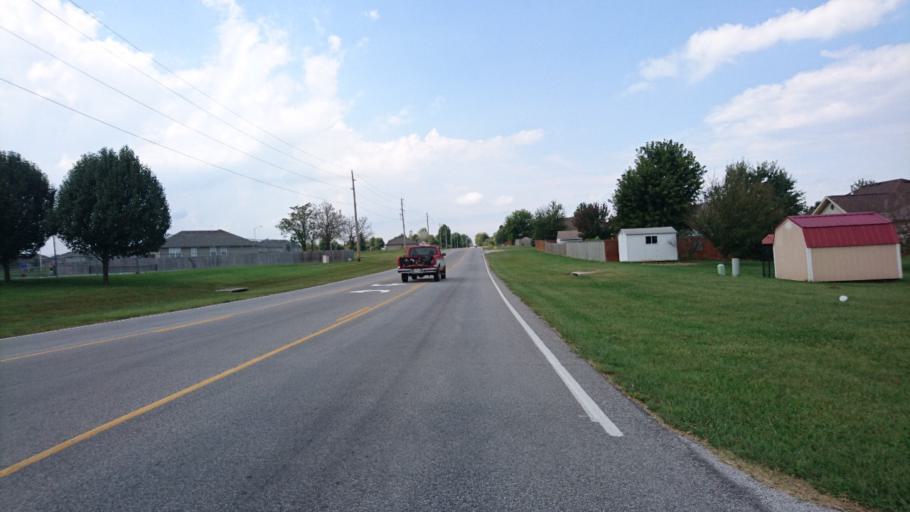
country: US
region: Missouri
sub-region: Greene County
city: Battlefield
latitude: 37.1981
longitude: -93.3936
